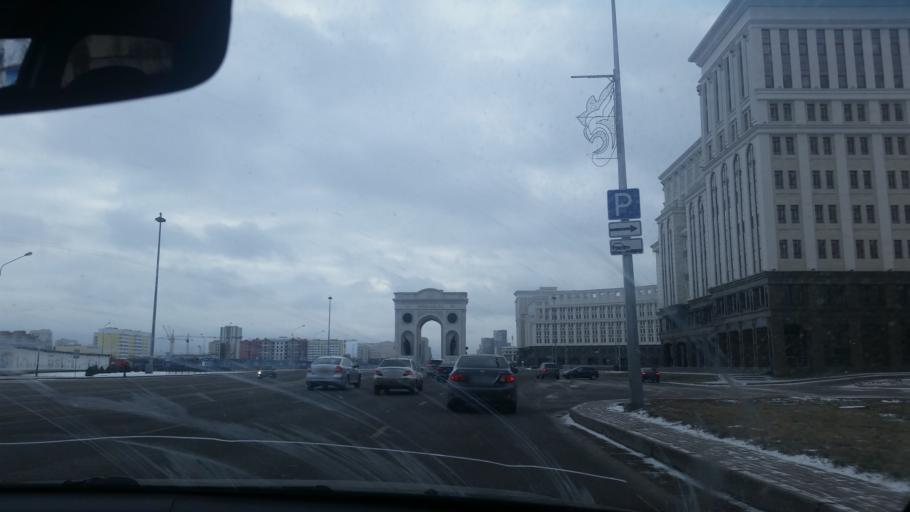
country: KZ
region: Astana Qalasy
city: Astana
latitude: 51.1063
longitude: 71.4306
